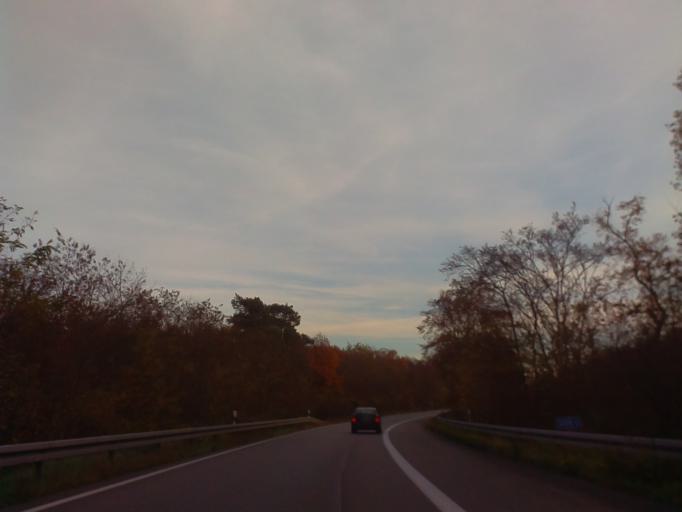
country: DE
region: Hesse
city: Viernheim
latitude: 49.5548
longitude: 8.5556
